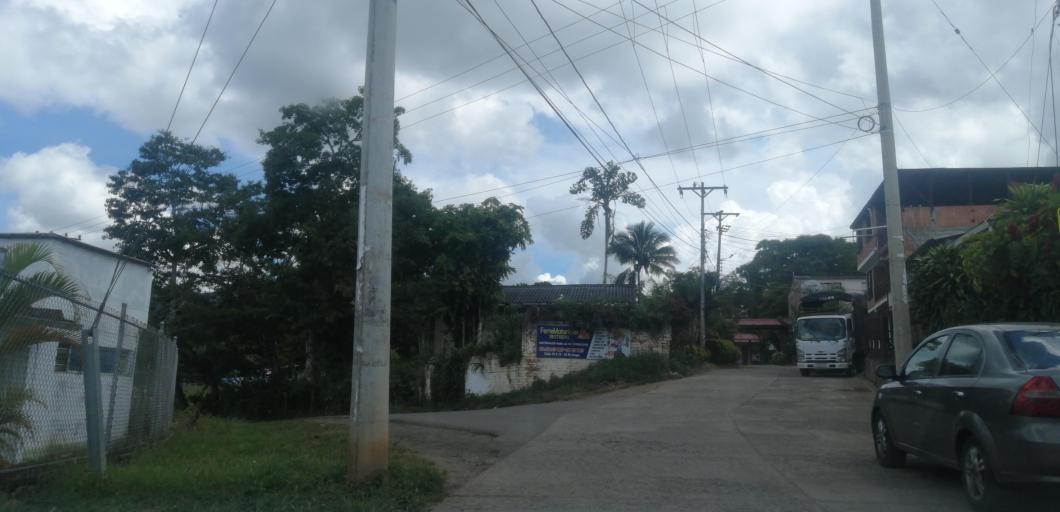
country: CO
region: Valle del Cauca
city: Restrepo
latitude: 3.8217
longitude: -76.5264
